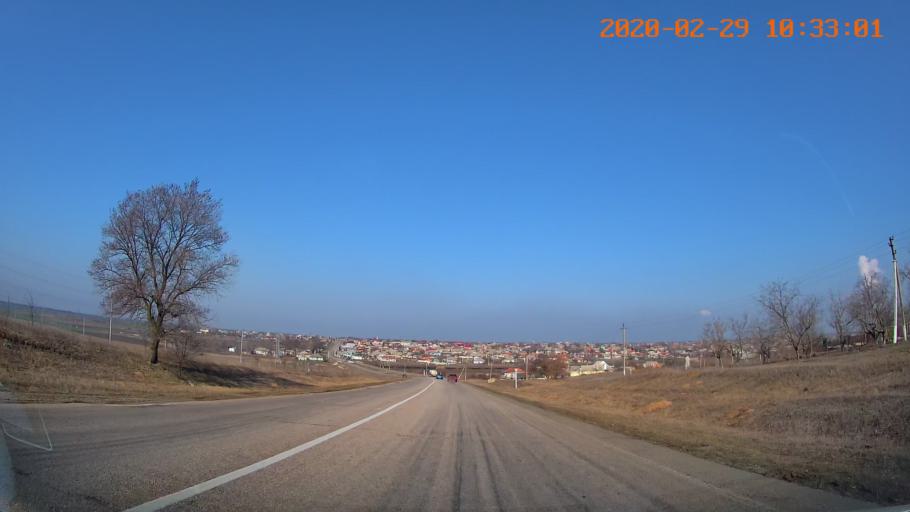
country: UA
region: Odessa
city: Velykoploske
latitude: 46.9675
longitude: 29.5493
